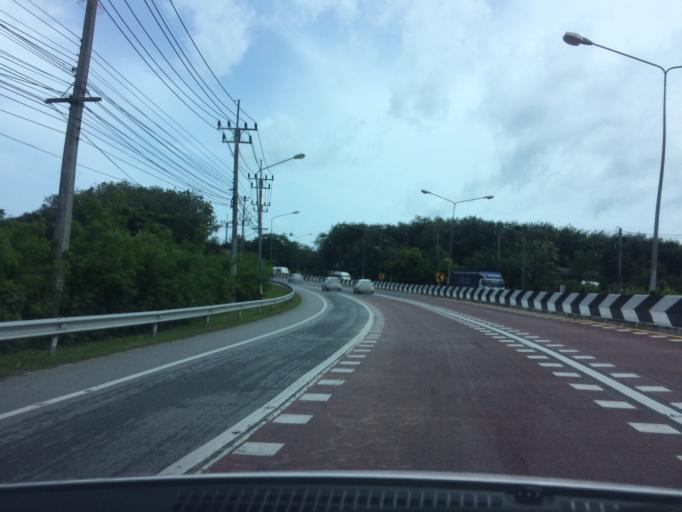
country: TH
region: Phuket
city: Thalang
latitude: 8.1550
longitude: 98.3379
